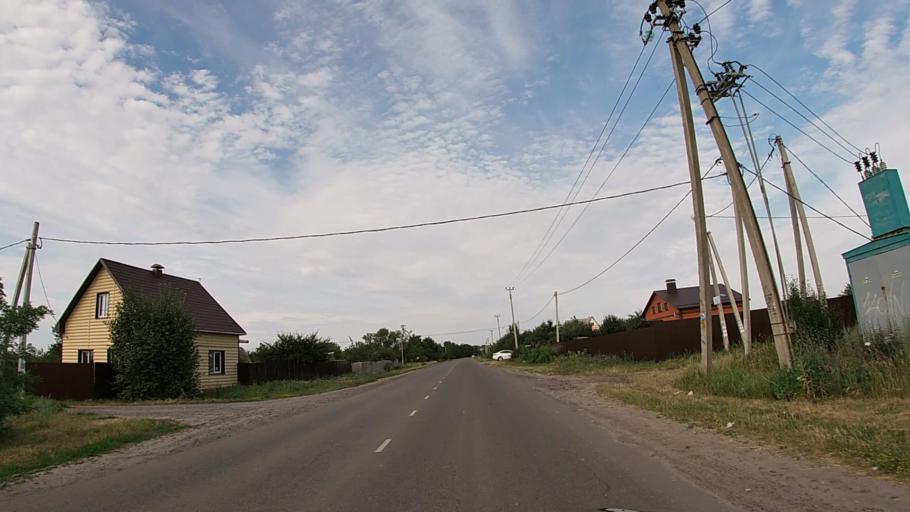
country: RU
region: Belgorod
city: Severnyy
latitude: 50.6971
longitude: 36.5750
